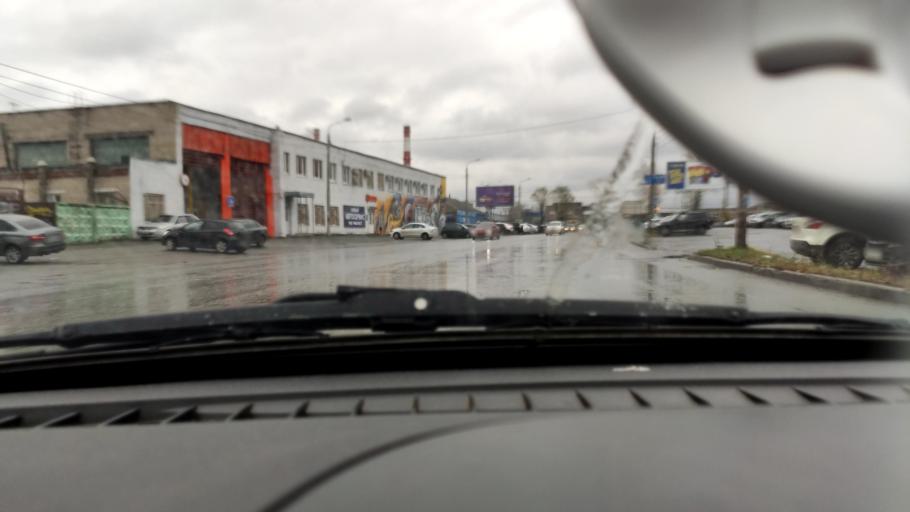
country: RU
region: Perm
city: Perm
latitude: 57.9752
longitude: 56.2438
